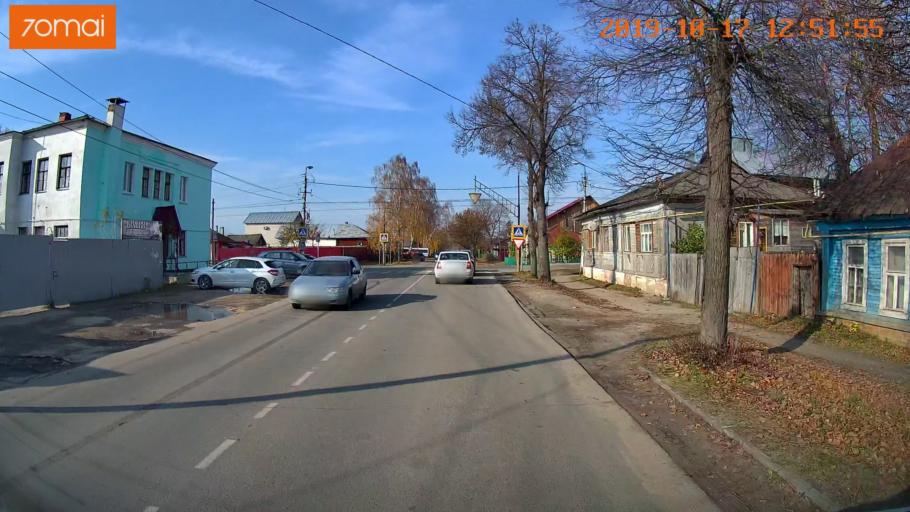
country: RU
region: Rjazan
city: Kasimov
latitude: 54.9424
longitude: 41.3894
